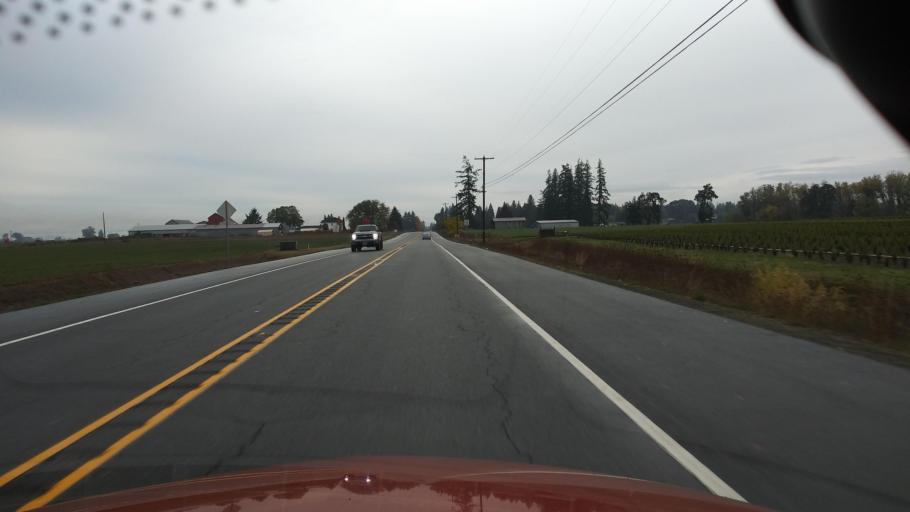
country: US
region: Oregon
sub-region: Washington County
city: Cornelius
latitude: 45.5324
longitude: -123.0597
